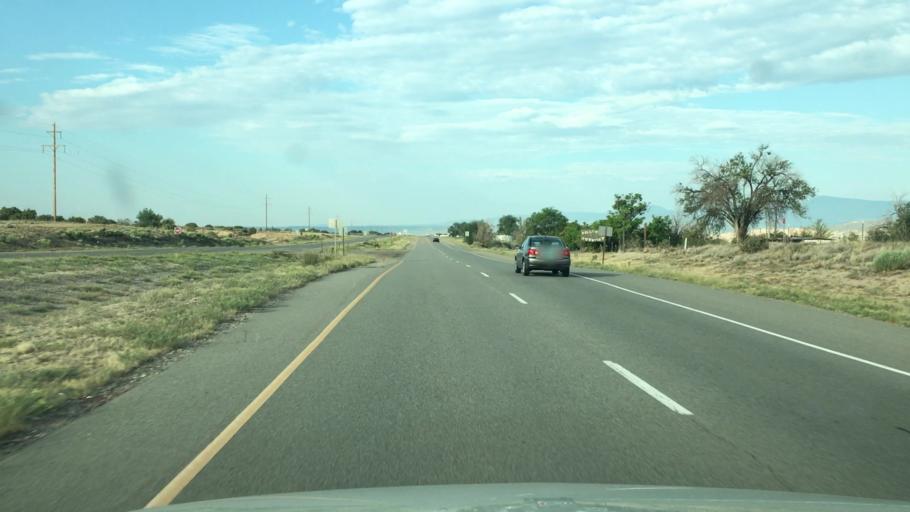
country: US
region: New Mexico
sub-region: Rio Arriba County
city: Ohkay Owingeh
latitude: 36.1267
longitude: -106.0071
